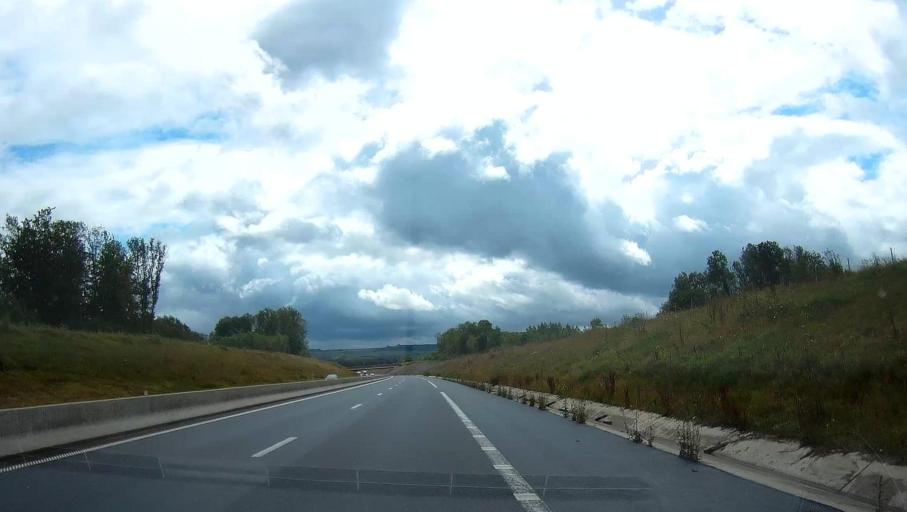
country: FR
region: Champagne-Ardenne
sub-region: Departement des Ardennes
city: Rimogne
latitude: 49.8199
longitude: 4.5142
